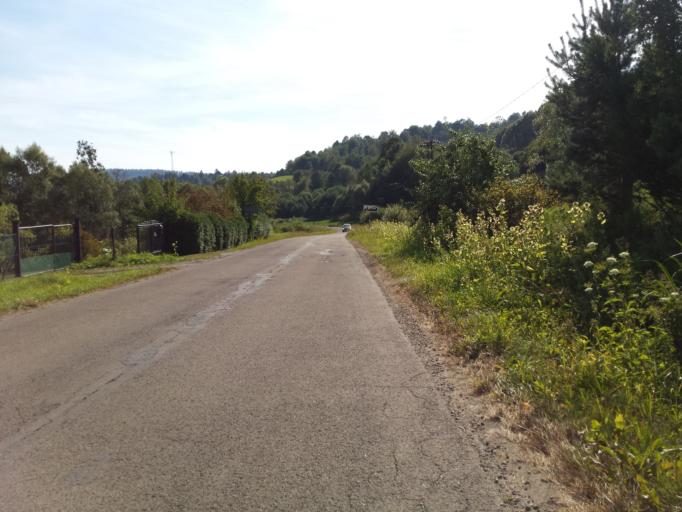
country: PL
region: Subcarpathian Voivodeship
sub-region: Powiat leski
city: Olszanica
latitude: 49.5265
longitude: 22.4895
